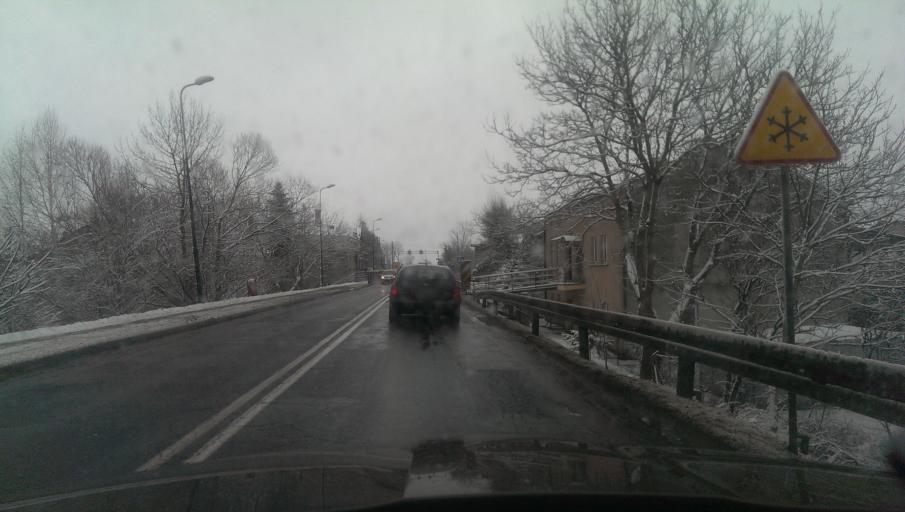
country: PL
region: Subcarpathian Voivodeship
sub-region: Powiat krosnienski
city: Rymanow
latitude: 49.5758
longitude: 21.8706
